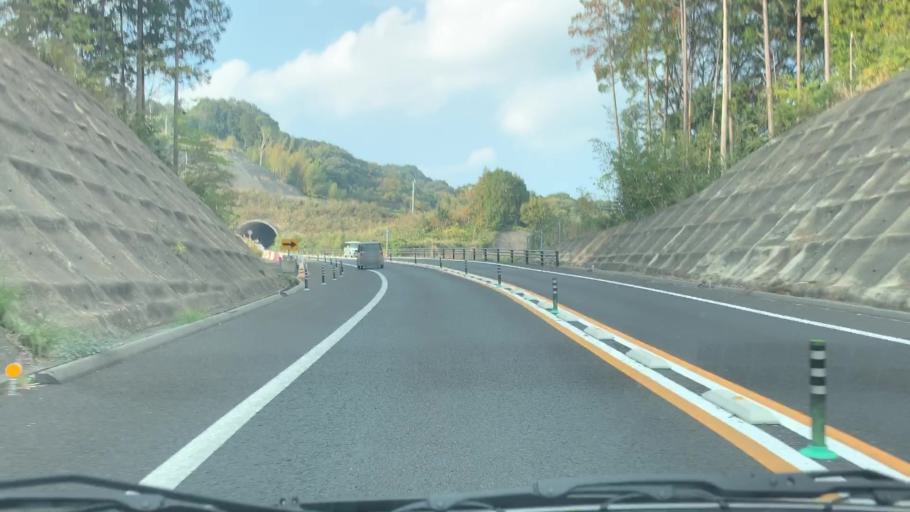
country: JP
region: Nagasaki
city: Sasebo
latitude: 32.9972
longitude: 129.7287
